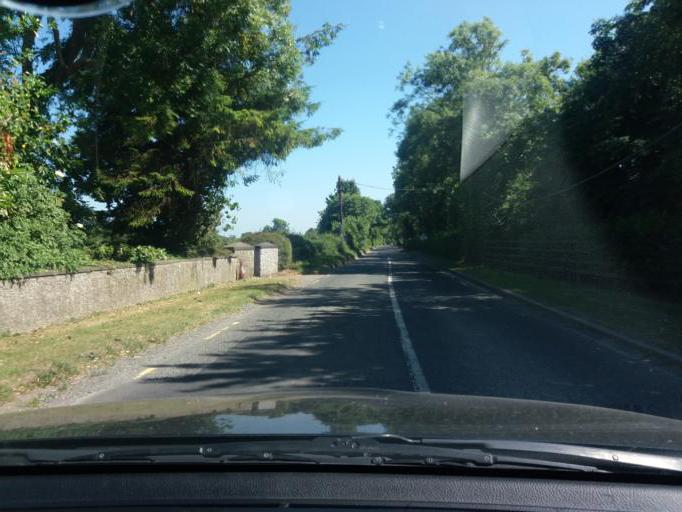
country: IE
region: Leinster
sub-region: Fingal County
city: Swords
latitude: 53.4622
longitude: -6.2713
